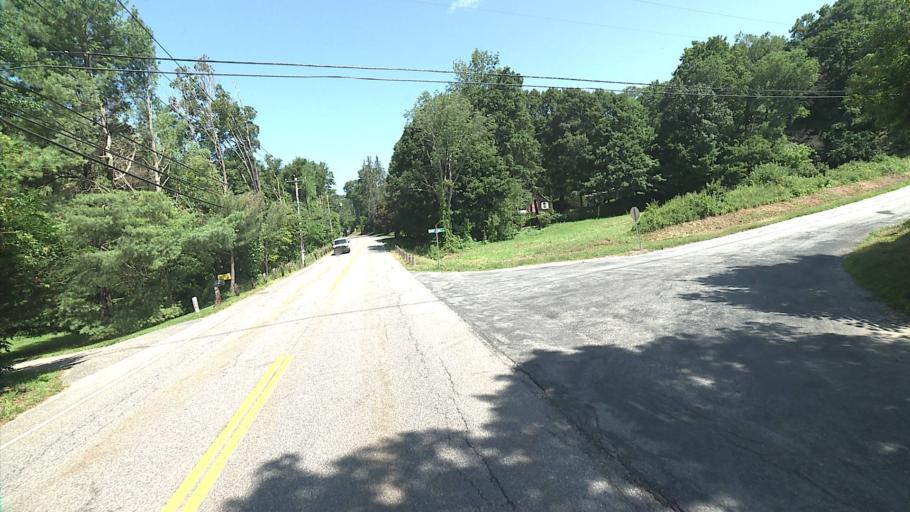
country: US
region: Connecticut
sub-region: Litchfield County
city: New Preston
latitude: 41.7008
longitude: -73.3446
